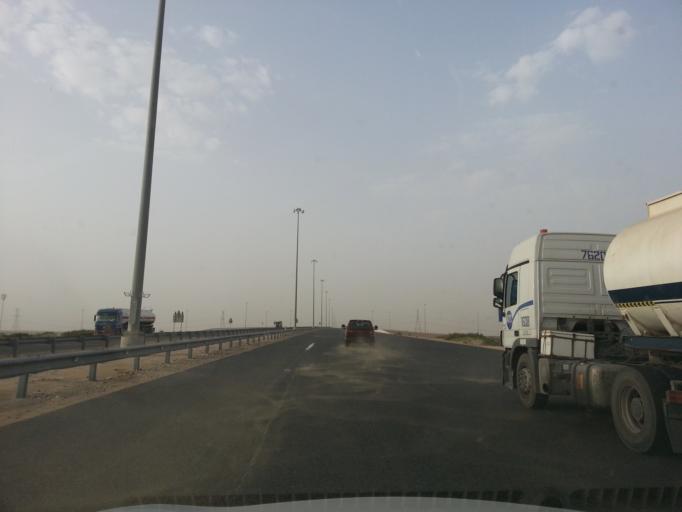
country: AE
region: Dubai
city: Dubai
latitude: 24.5966
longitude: 55.1222
